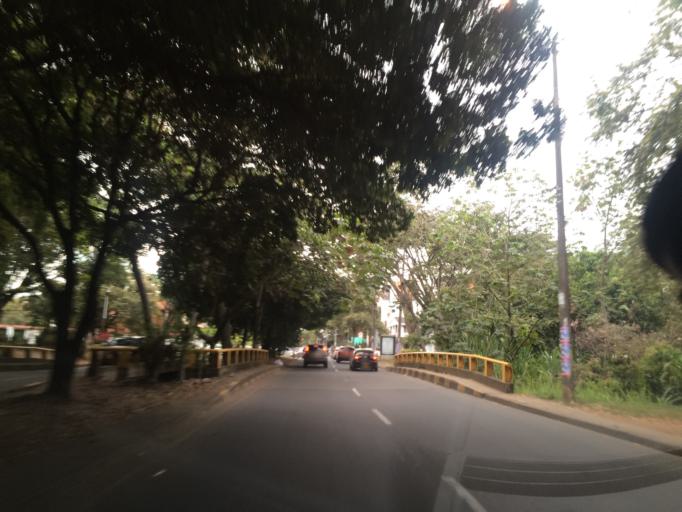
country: CO
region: Valle del Cauca
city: Cali
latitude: 3.3677
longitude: -76.5371
